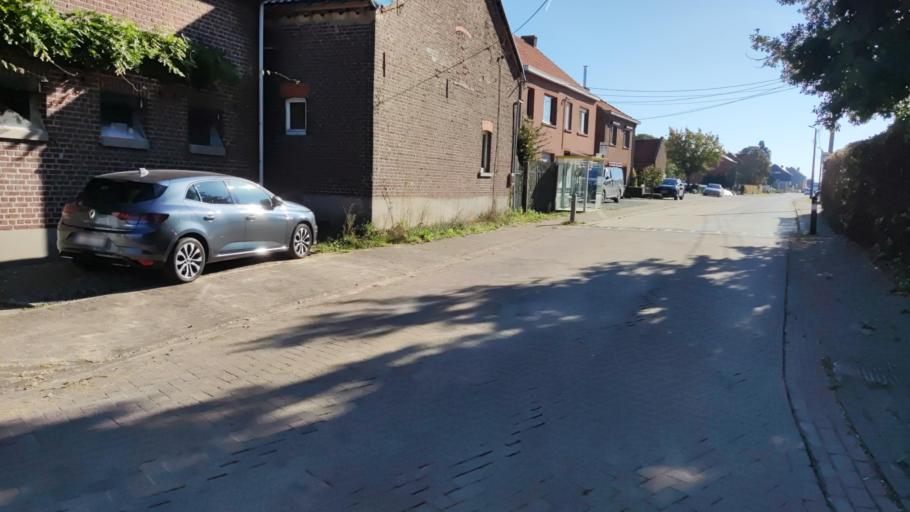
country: BE
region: Flanders
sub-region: Provincie Vlaams-Brabant
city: Tienen
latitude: 50.8152
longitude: 5.0056
